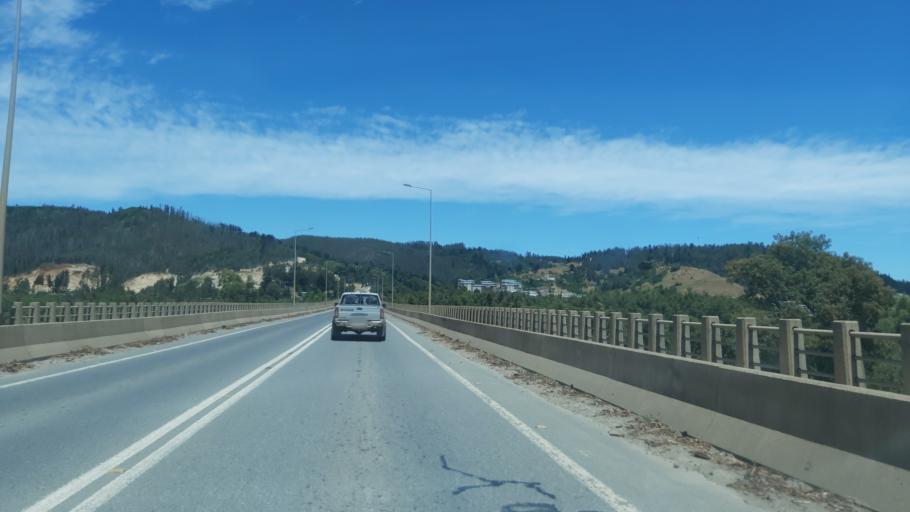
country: CL
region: Maule
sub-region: Provincia de Talca
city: Constitucion
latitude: -35.3376
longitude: -72.3900
